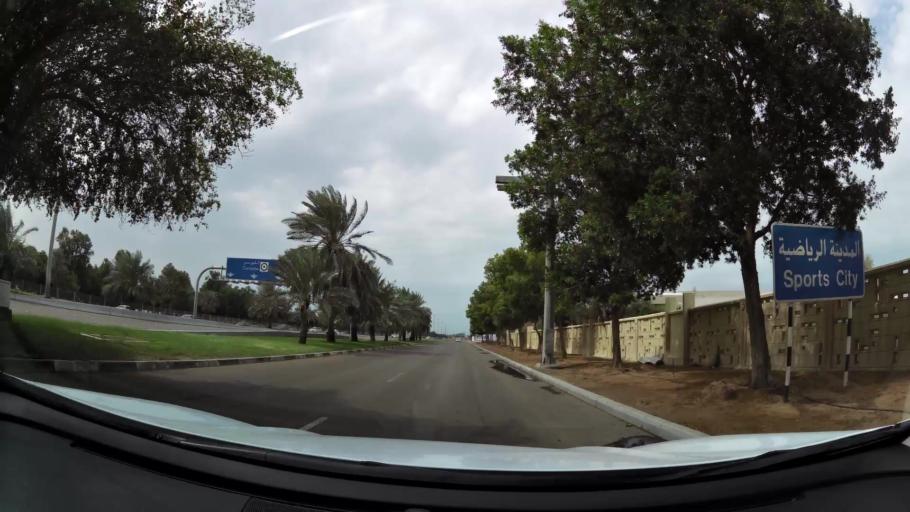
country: AE
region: Abu Dhabi
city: Abu Dhabi
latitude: 24.4124
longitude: 54.4550
